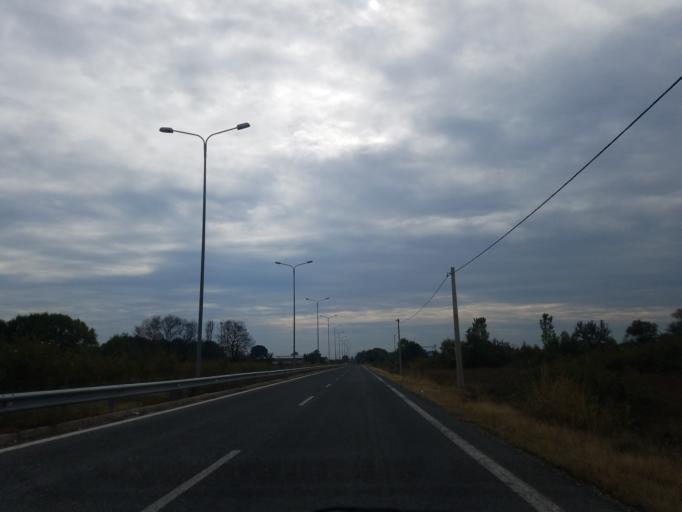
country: GR
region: Thessaly
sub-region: Trikala
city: Pyrgetos
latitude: 39.5332
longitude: 21.7404
